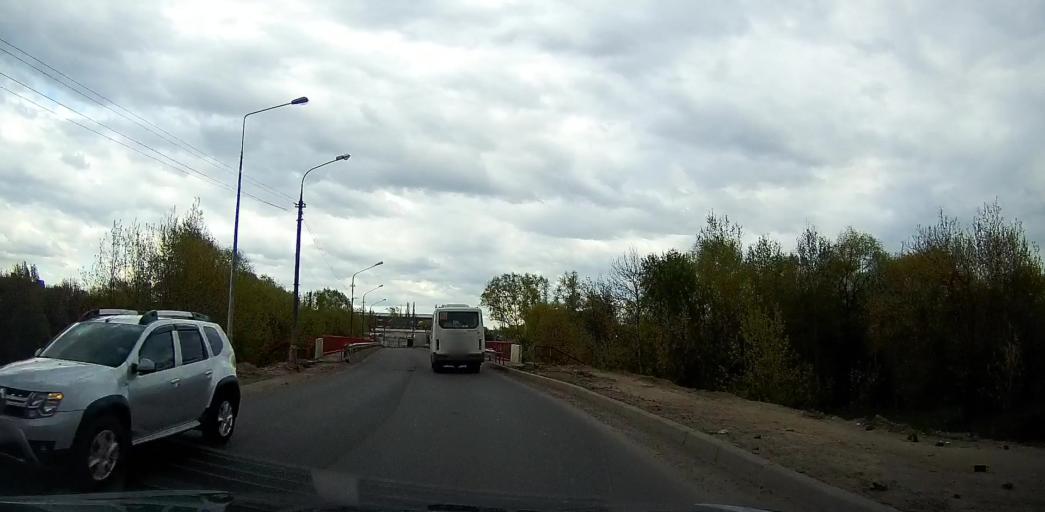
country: RU
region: Moskovskaya
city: Pavlovskiy Posad
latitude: 55.7806
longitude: 38.6879
